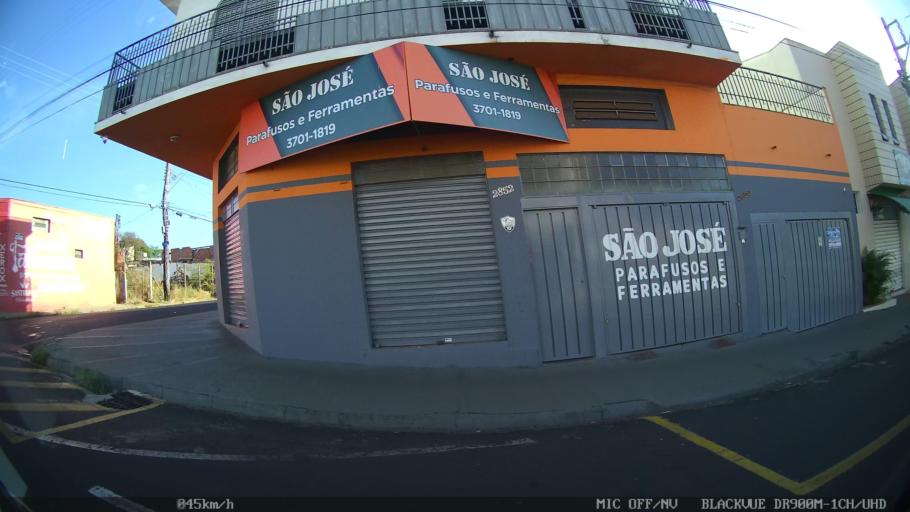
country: BR
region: Sao Paulo
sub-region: Franca
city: Franca
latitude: -20.5405
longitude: -47.3881
